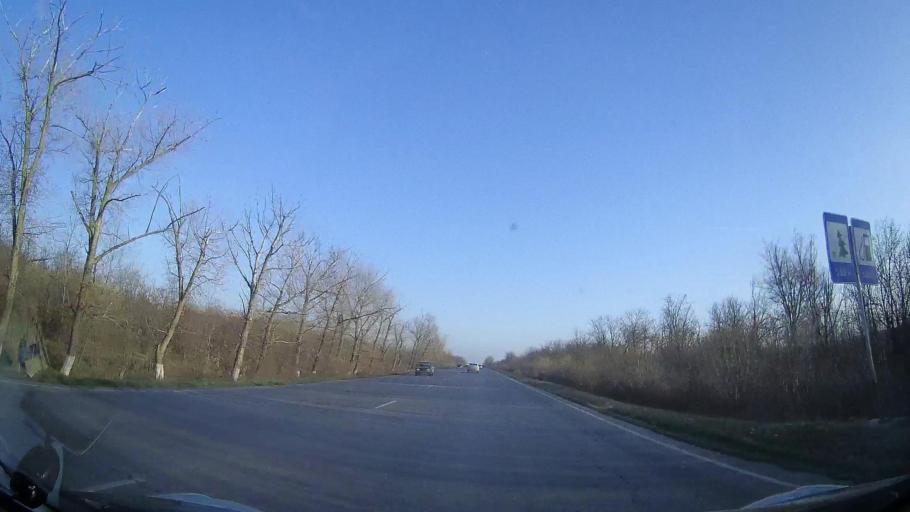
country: RU
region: Rostov
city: Bataysk
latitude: 47.0673
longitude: 39.8027
